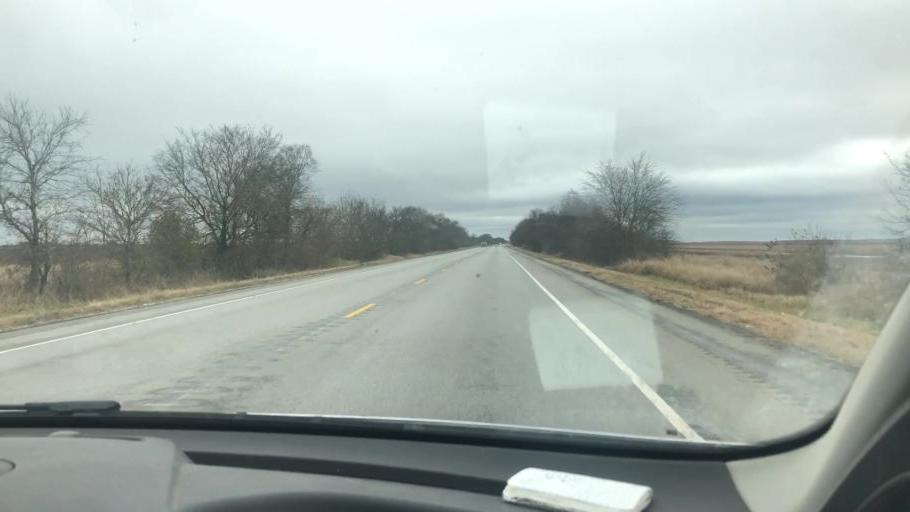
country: US
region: Texas
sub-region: Matagorda County
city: Van Vleck
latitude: 29.1226
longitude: -95.9814
